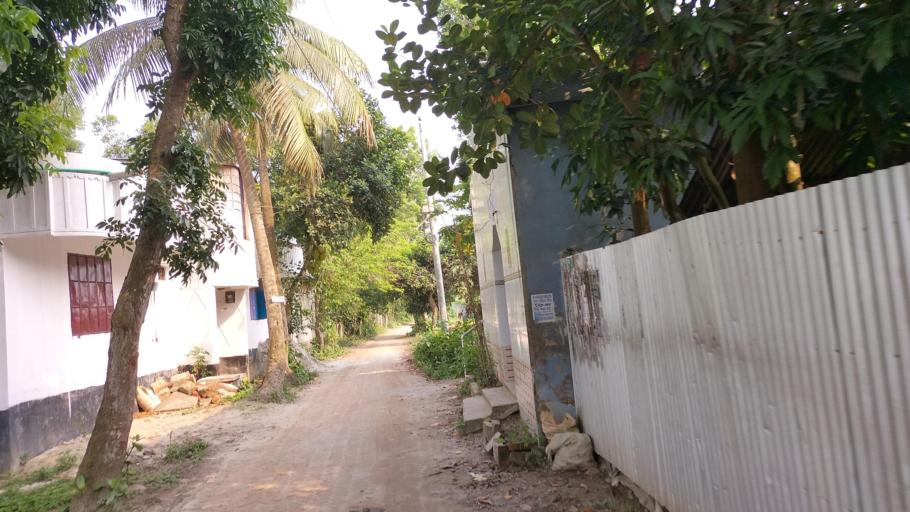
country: BD
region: Dhaka
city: Azimpur
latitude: 23.6719
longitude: 90.3134
